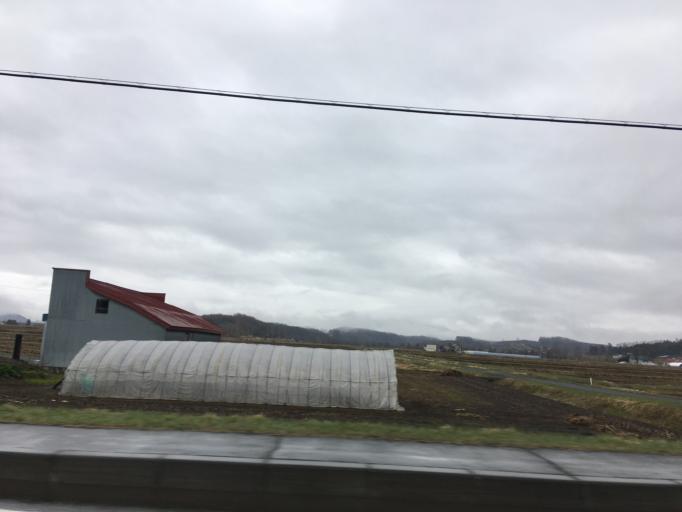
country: JP
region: Hokkaido
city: Nayoro
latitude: 44.1165
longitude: 142.4808
